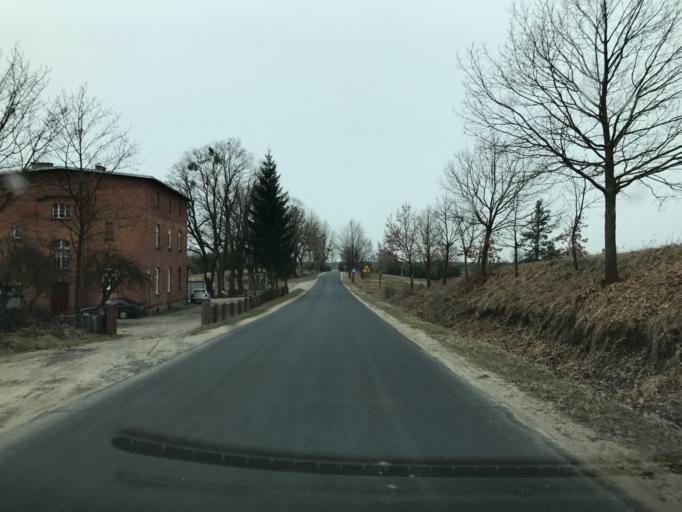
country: PL
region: Kujawsko-Pomorskie
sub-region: Powiat brodnicki
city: Gorzno
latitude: 53.1764
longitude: 19.6395
